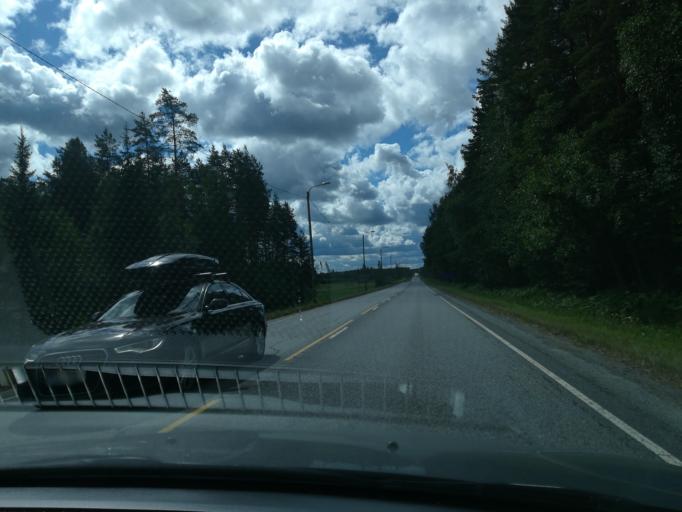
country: FI
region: Southern Savonia
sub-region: Mikkeli
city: Ristiina
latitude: 61.4984
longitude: 27.2396
